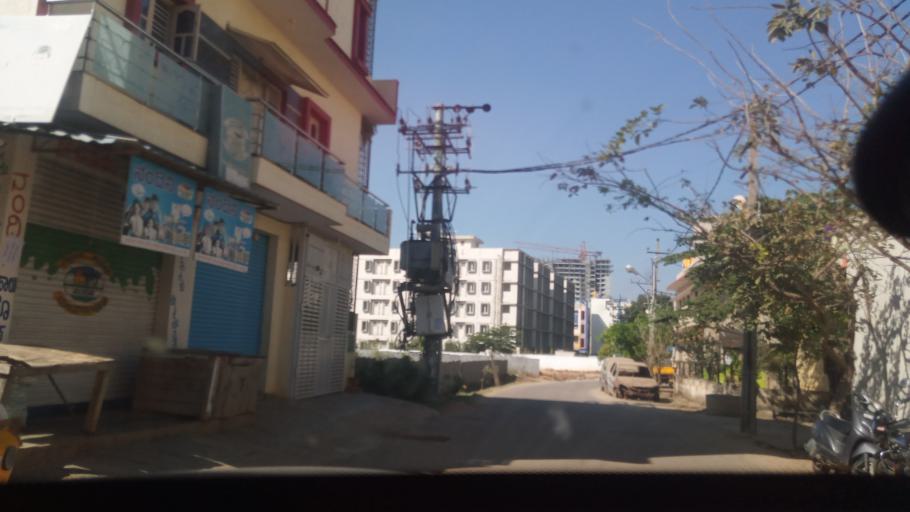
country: IN
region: Karnataka
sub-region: Bangalore Urban
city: Yelahanka
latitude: 13.0411
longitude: 77.5014
